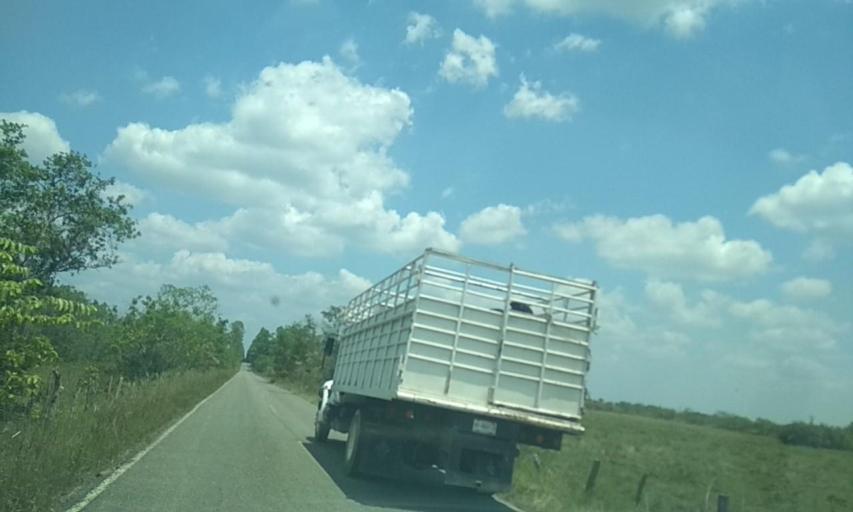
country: MX
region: Tabasco
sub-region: Huimanguillo
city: Francisco Rueda
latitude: 17.7670
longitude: -93.7982
